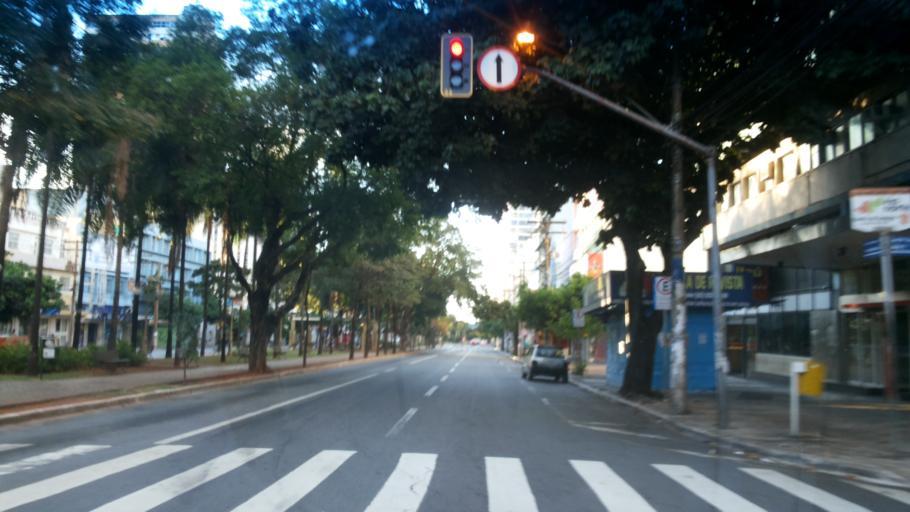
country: BR
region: Goias
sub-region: Goiania
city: Goiania
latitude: -16.6774
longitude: -49.2572
